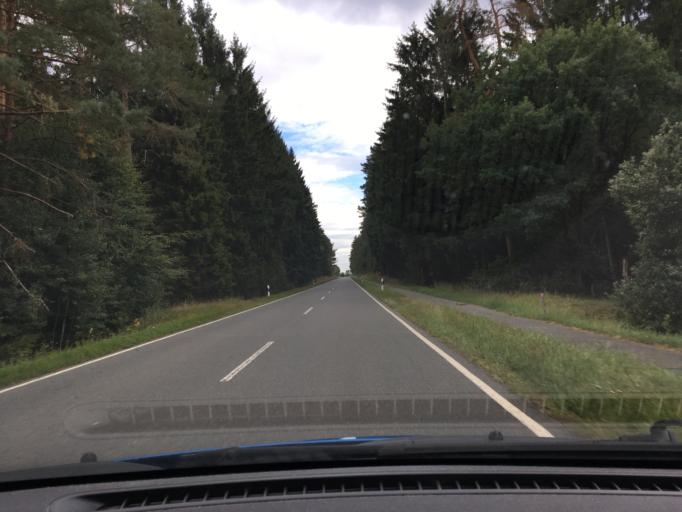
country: DE
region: Lower Saxony
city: Jesteburg
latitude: 53.2523
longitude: 9.9158
